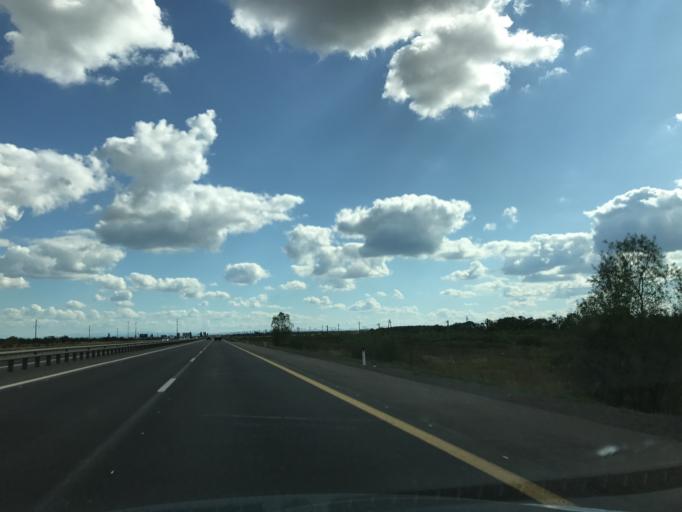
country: RU
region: Adygeya
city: Adygeysk
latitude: 44.8222
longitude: 39.2255
